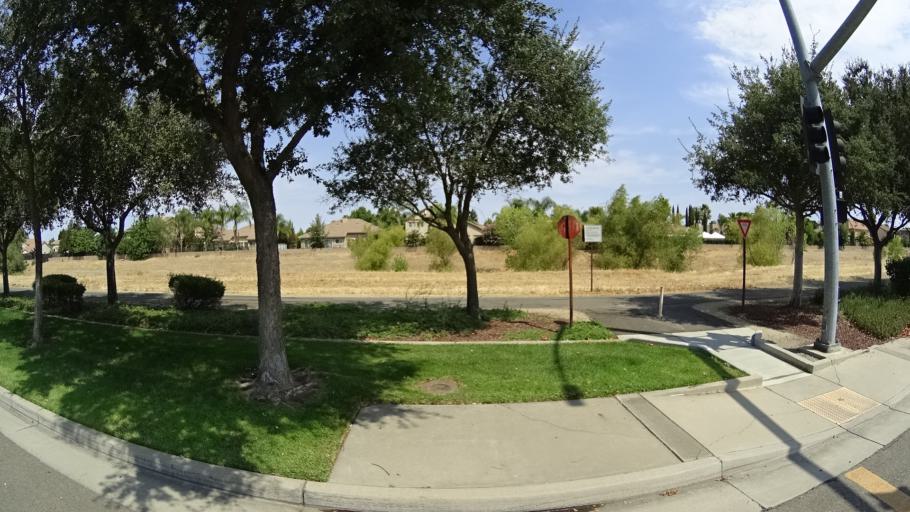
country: US
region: California
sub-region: Sacramento County
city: Laguna
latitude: 38.3940
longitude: -121.4270
